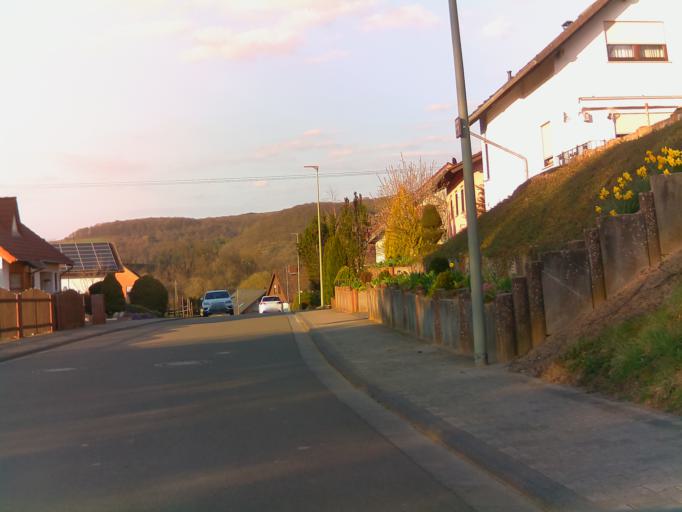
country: DE
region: Rheinland-Pfalz
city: Rehborn
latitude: 49.7332
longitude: 7.6895
